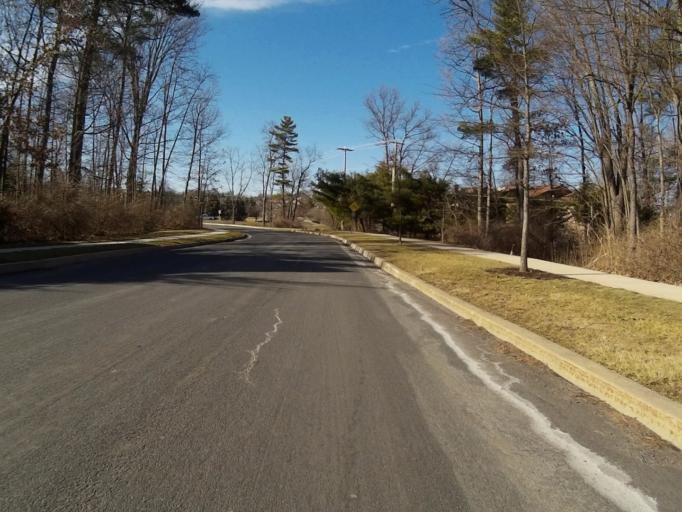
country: US
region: Pennsylvania
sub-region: Centre County
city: State College
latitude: 40.7971
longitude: -77.8862
